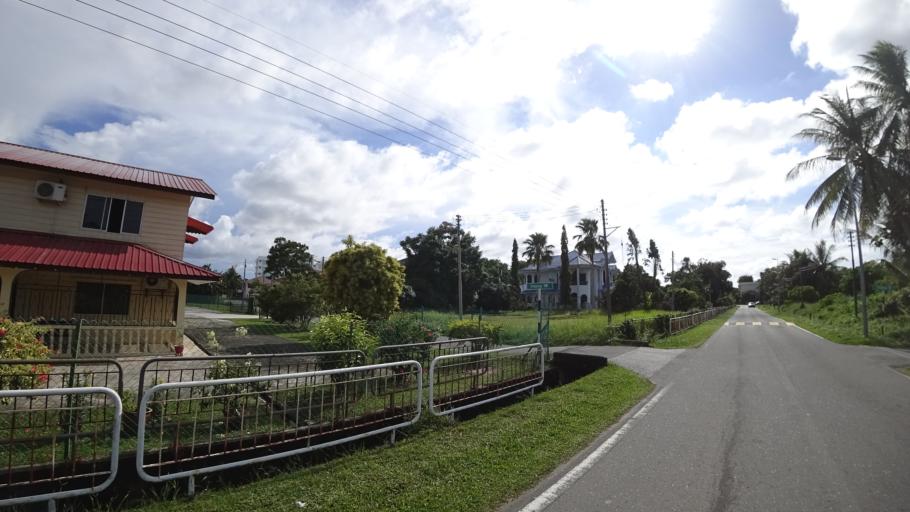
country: BN
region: Brunei and Muara
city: Bandar Seri Begawan
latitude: 4.9368
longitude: 114.9466
